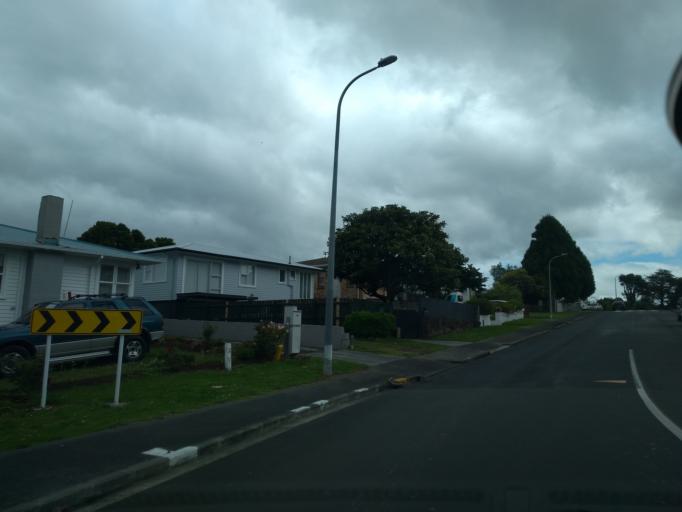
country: NZ
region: Auckland
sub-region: Auckland
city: Tamaki
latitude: -36.9122
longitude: 174.8242
